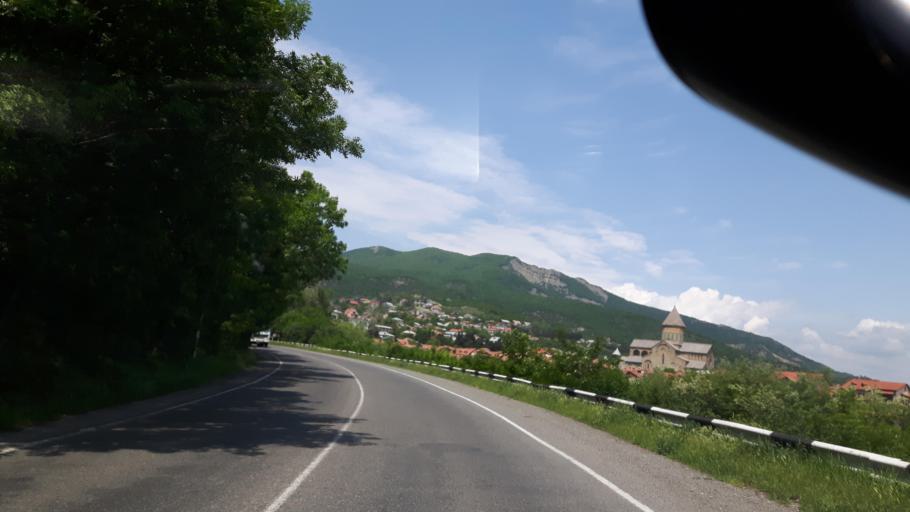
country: GE
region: Mtskheta-Mtianeti
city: Mtskheta
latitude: 41.8382
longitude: 44.7231
